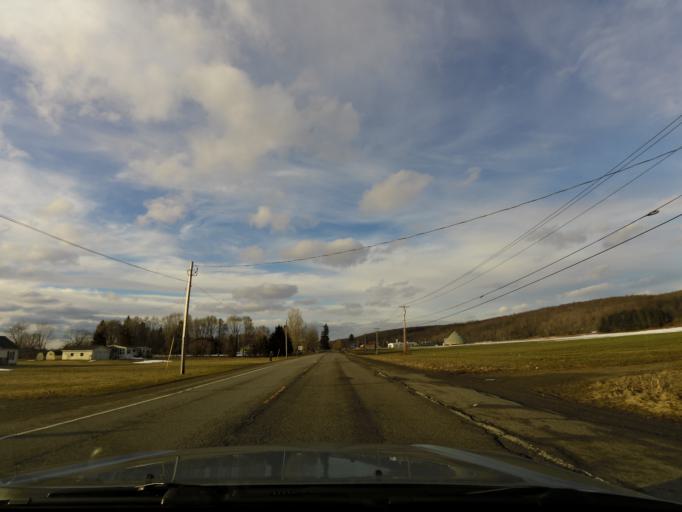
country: US
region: New York
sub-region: Cattaraugus County
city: Franklinville
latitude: 42.3510
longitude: -78.4531
